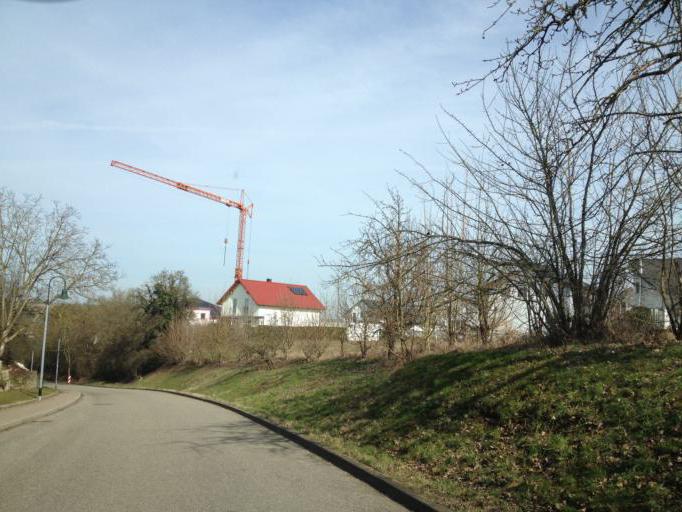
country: DE
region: Baden-Wuerttemberg
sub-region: Regierungsbezirk Stuttgart
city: Oedheim
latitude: 49.2380
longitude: 9.2611
